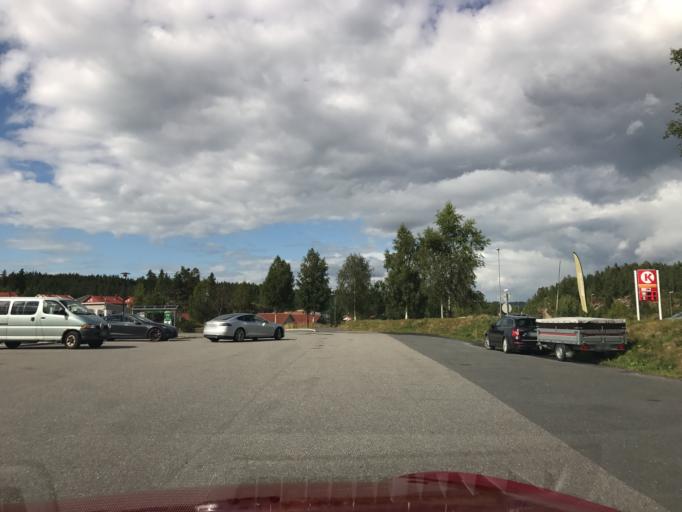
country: NO
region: Aust-Agder
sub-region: Gjerstad
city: Gjerstad
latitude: 58.8204
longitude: 9.0739
